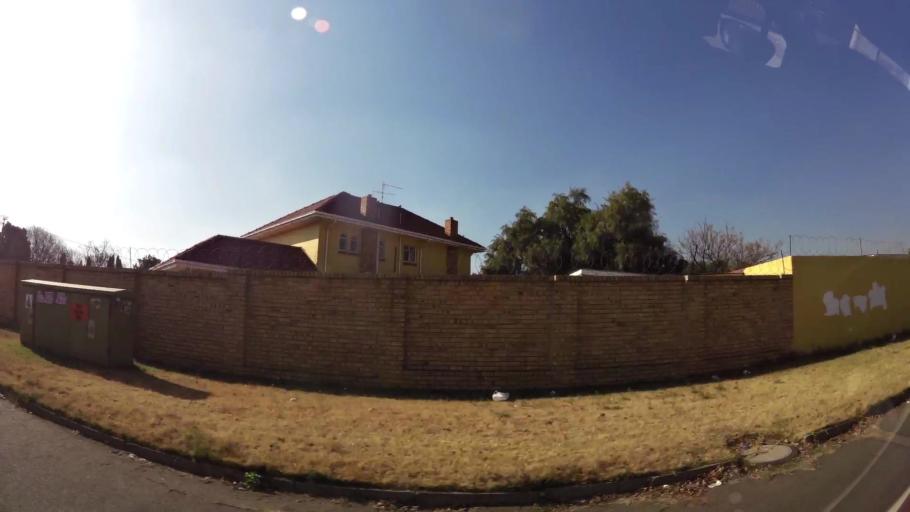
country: ZA
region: Gauteng
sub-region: West Rand District Municipality
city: Randfontein
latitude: -26.1684
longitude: 27.7100
